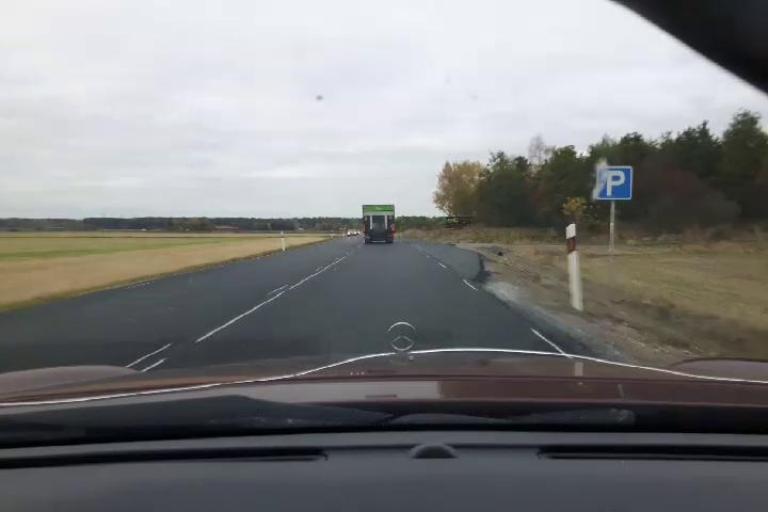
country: SE
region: Uppsala
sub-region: Enkopings Kommun
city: Enkoping
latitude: 59.6284
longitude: 17.0476
